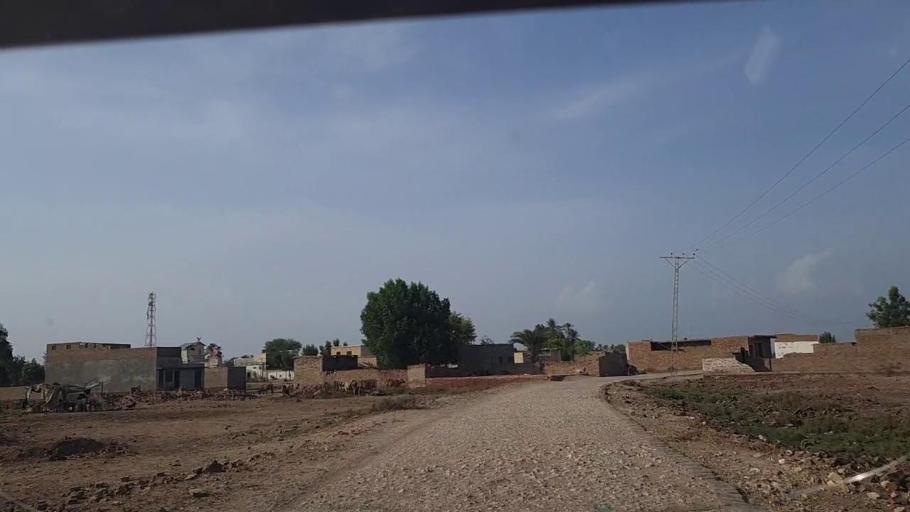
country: PK
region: Sindh
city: Ghotki
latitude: 28.0128
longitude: 69.2938
